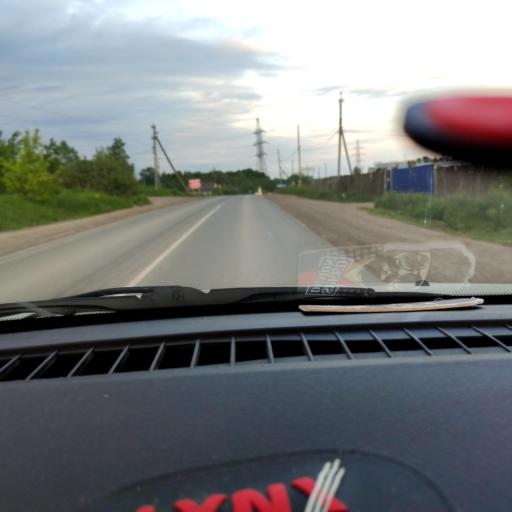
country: RU
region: Perm
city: Froly
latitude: 57.9200
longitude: 56.2890
